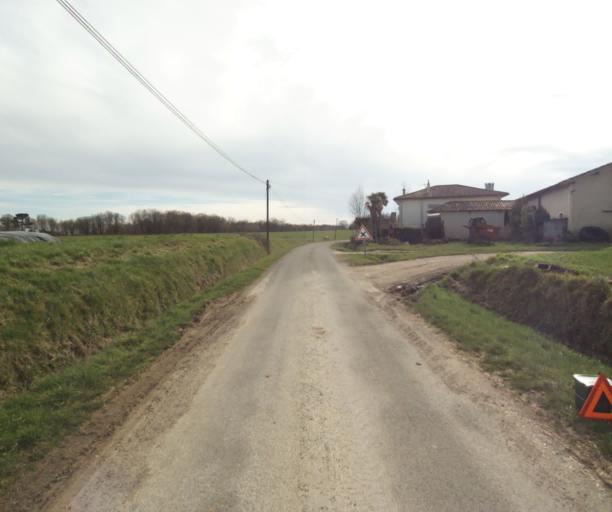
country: FR
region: Aquitaine
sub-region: Departement des Landes
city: Gabarret
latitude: 43.9320
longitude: 0.0458
